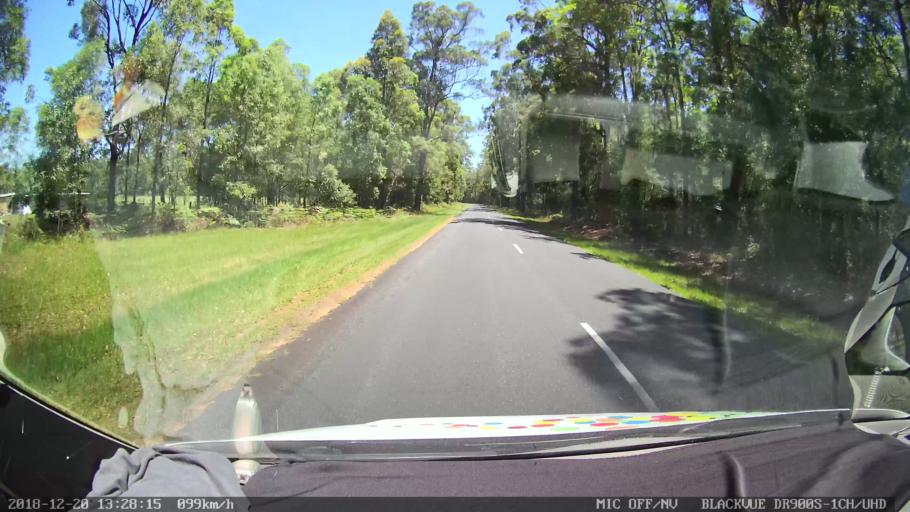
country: AU
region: New South Wales
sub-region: Clarence Valley
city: Gordon
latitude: -29.1720
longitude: 152.9911
